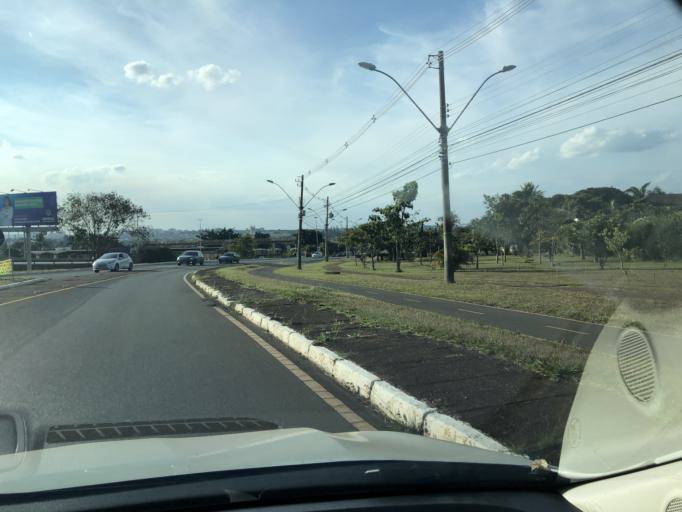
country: BR
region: Federal District
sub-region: Brasilia
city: Brasilia
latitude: -15.8818
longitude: -47.9589
